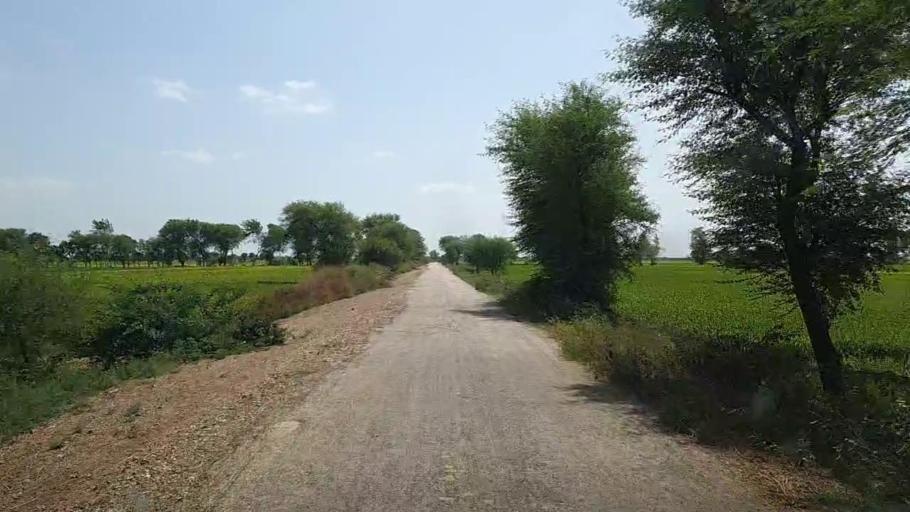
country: PK
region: Sindh
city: Kario
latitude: 24.6477
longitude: 68.5640
